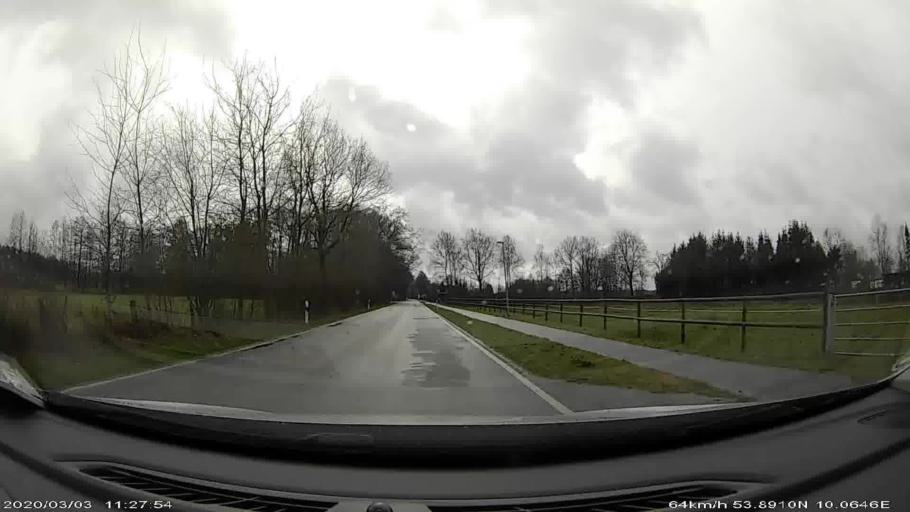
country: DE
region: Schleswig-Holstein
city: Hartenholm
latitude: 53.8888
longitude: 10.0658
